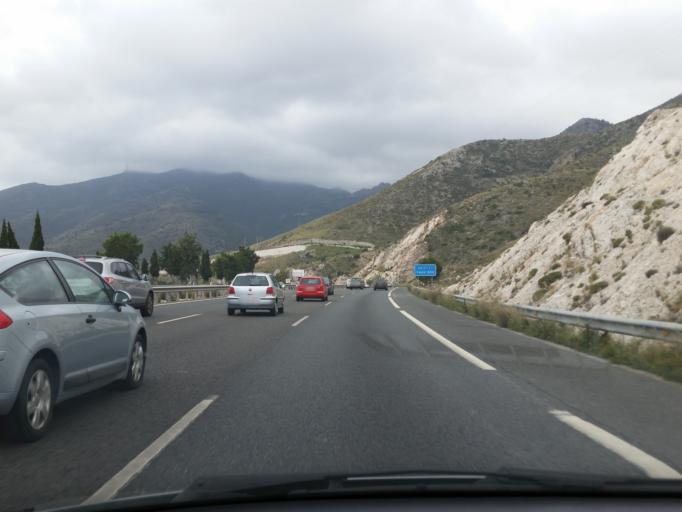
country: ES
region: Andalusia
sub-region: Provincia de Malaga
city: Benalmadena
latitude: 36.6061
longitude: -4.5509
